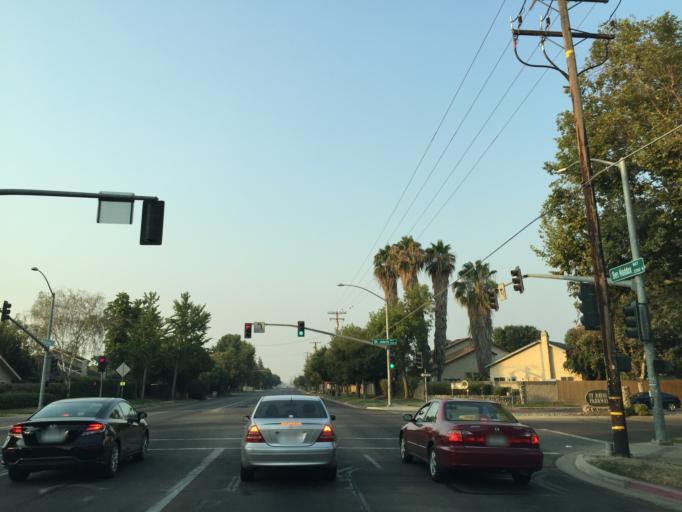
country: US
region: California
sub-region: Tulare County
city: Visalia
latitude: 36.3507
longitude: -119.2790
